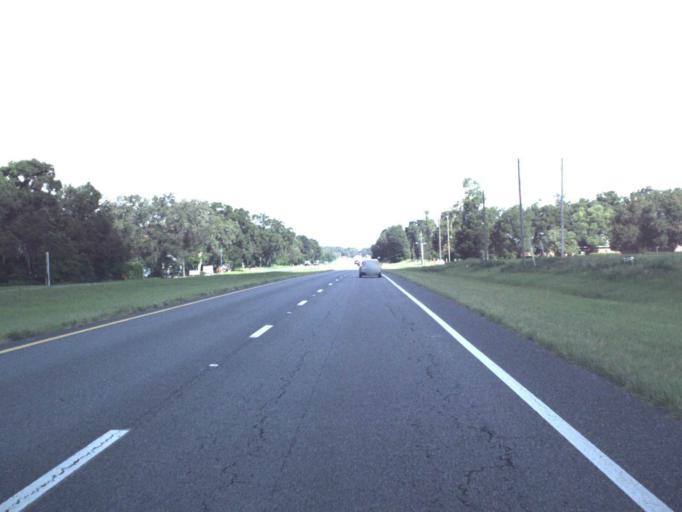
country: US
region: Florida
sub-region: Alachua County
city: High Springs
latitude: 29.8144
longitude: -82.5678
